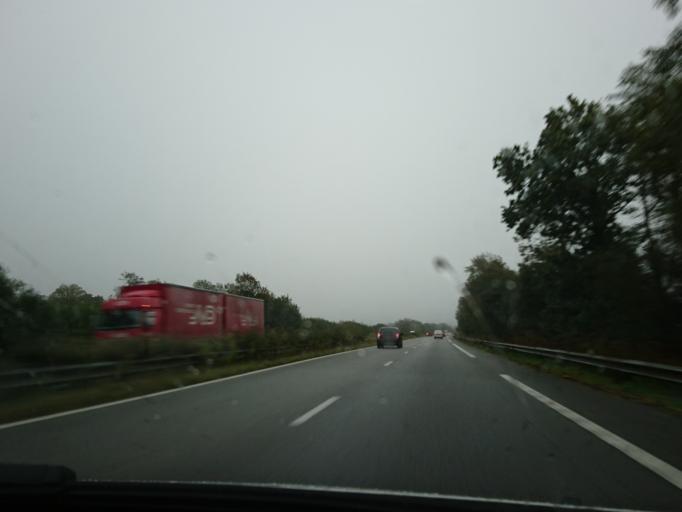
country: FR
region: Brittany
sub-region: Departement du Finistere
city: Saint-Yvi
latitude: 47.9657
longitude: -3.9746
